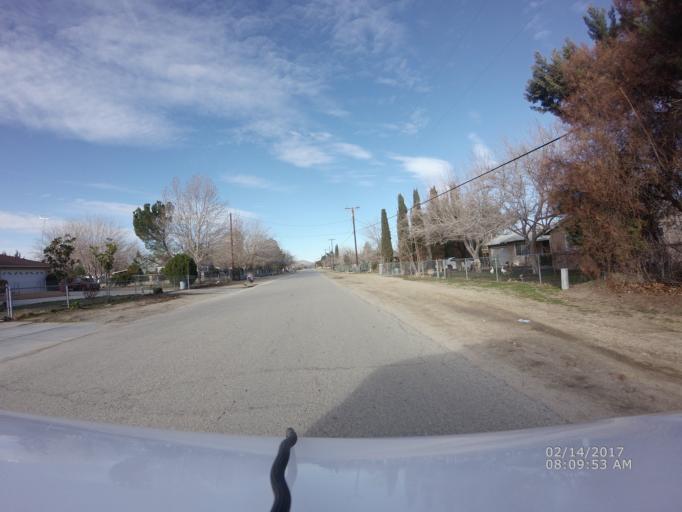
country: US
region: California
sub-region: Los Angeles County
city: Littlerock
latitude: 34.5538
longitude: -117.9526
